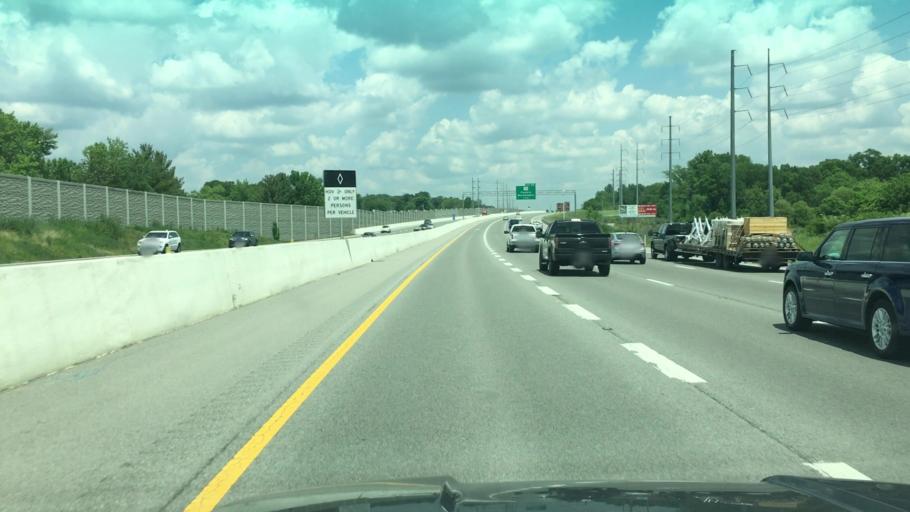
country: US
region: Tennessee
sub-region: Williamson County
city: Franklin
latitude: 35.8947
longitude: -86.8289
